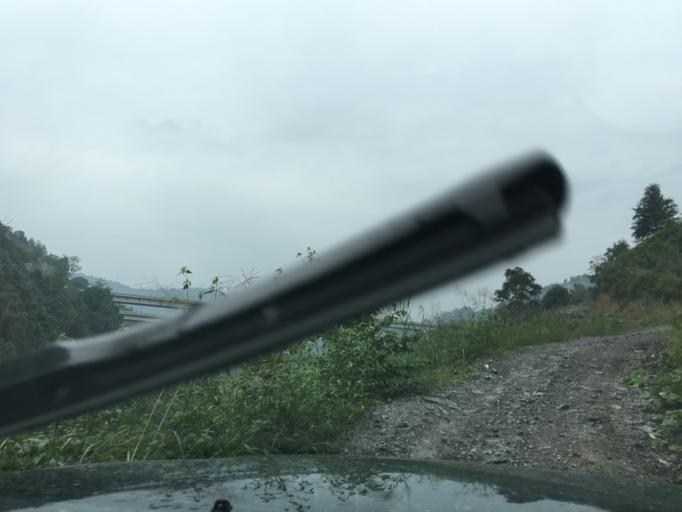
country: CN
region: Guangxi Zhuangzu Zizhiqu
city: Xinzhou
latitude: 25.0524
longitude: 105.9193
